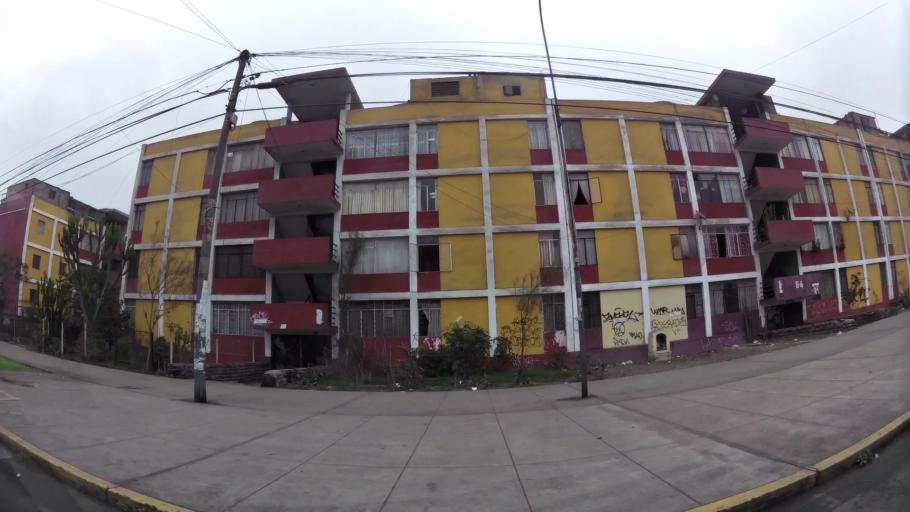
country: PE
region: Lima
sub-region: Lima
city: San Luis
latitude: -12.0727
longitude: -77.0215
